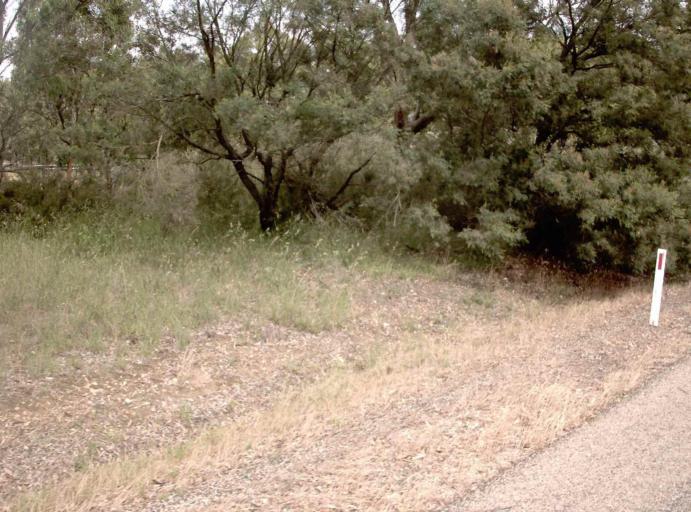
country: AU
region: Victoria
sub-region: Wellington
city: Sale
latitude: -37.9286
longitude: 147.0912
